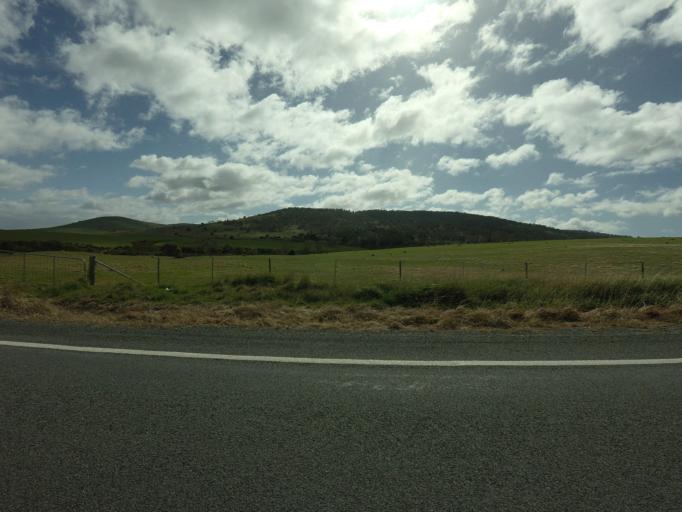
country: AU
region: Tasmania
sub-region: Northern Midlands
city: Evandale
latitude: -41.8160
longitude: 147.5703
